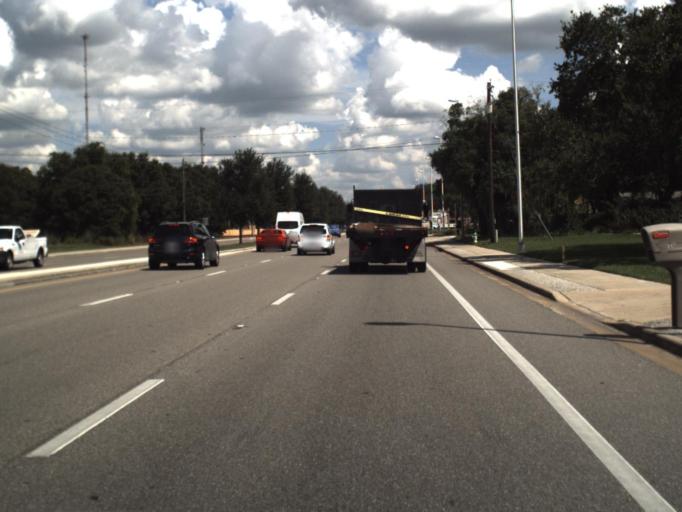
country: US
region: Florida
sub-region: Sarasota County
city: Fruitville
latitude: 27.3378
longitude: -82.4722
